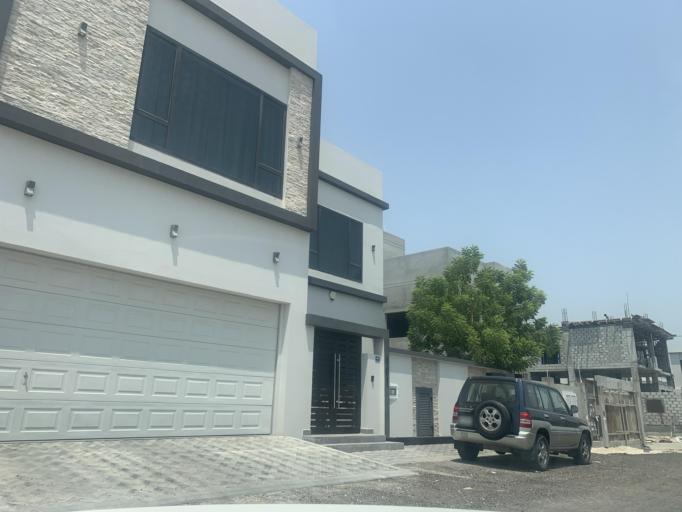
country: BH
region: Central Governorate
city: Madinat Hamad
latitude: 26.1433
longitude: 50.4663
